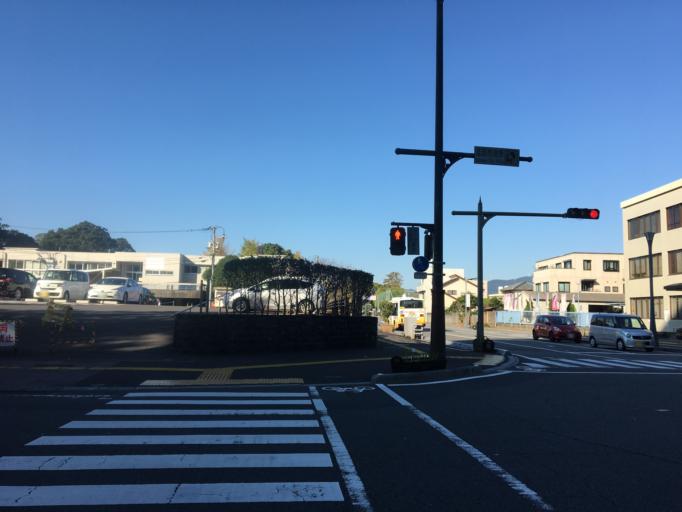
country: JP
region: Miyazaki
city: Nobeoka
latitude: 32.5824
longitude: 131.6647
